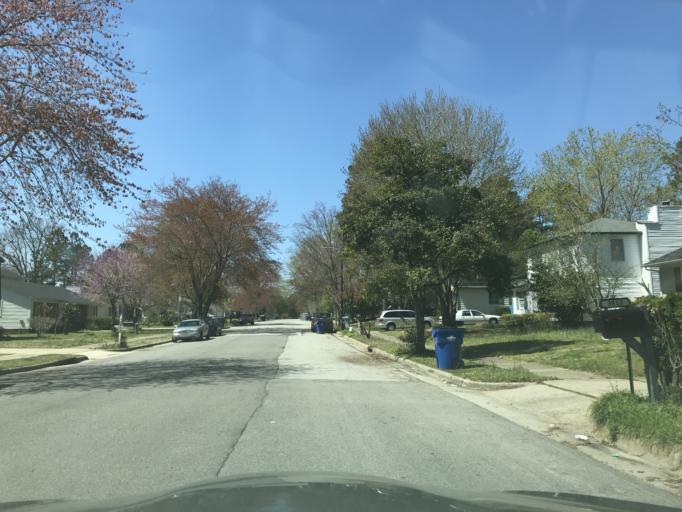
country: US
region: North Carolina
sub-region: Wake County
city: Raleigh
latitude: 35.8329
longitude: -78.5752
